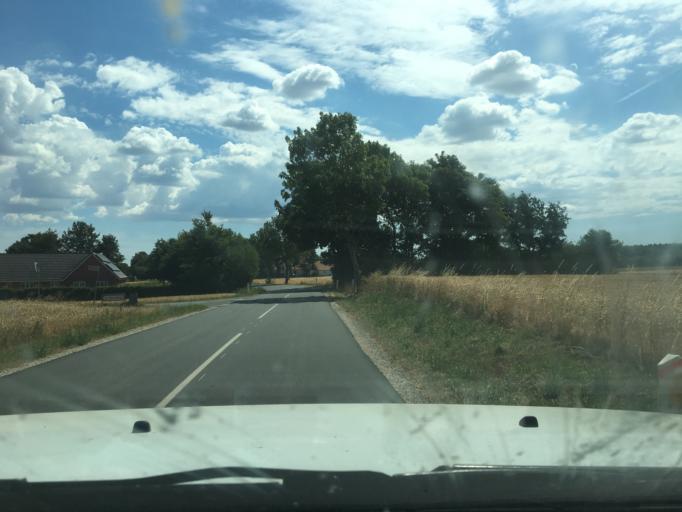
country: DK
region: Central Jutland
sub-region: Syddjurs Kommune
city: Hornslet
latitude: 56.3383
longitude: 10.2770
